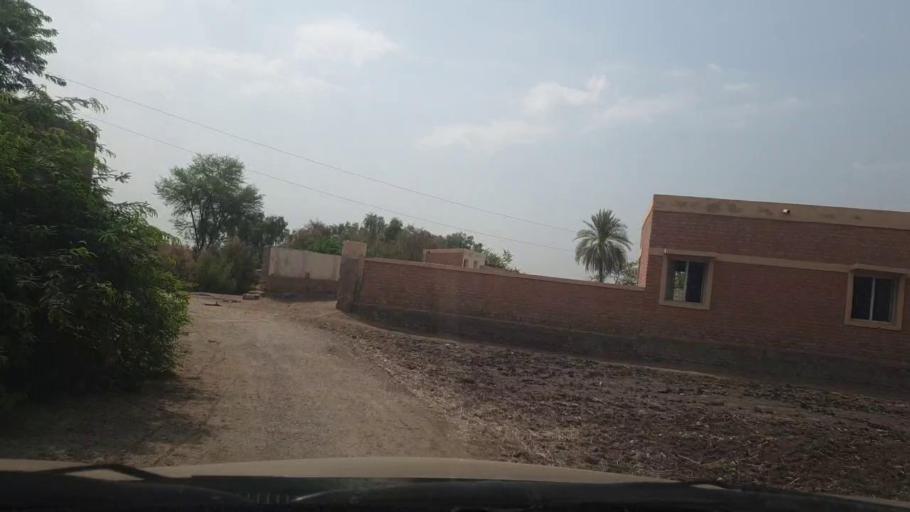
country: PK
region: Sindh
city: Larkana
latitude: 27.6799
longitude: 68.2023
